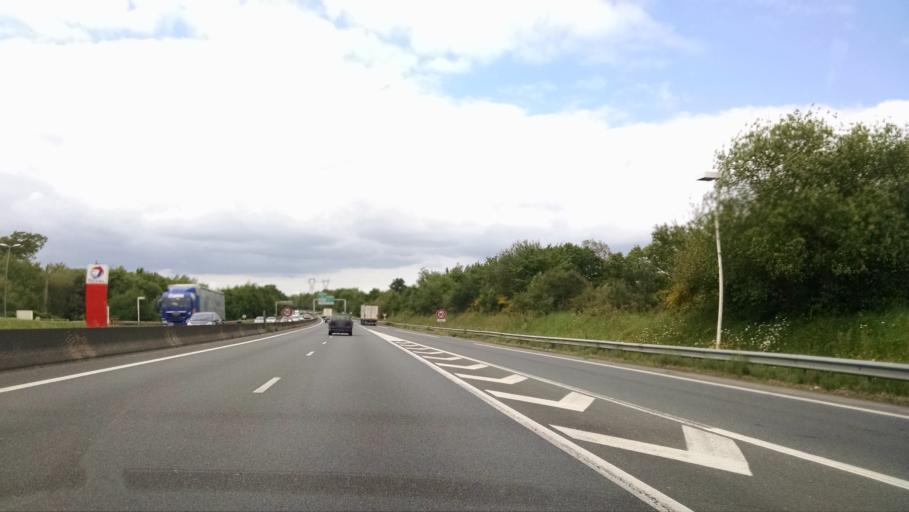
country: FR
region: Pays de la Loire
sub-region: Departement de la Loire-Atlantique
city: Les Sorinieres
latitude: 47.1613
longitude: -1.5128
